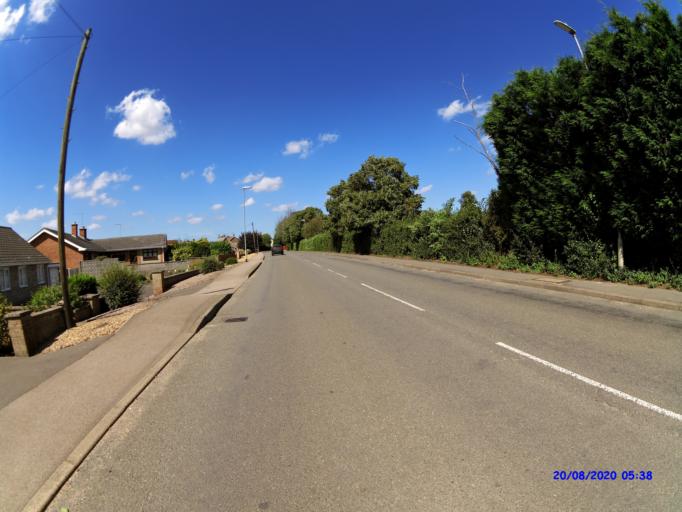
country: GB
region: England
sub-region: Cambridgeshire
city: Whittlesey
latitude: 52.5503
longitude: -0.1212
